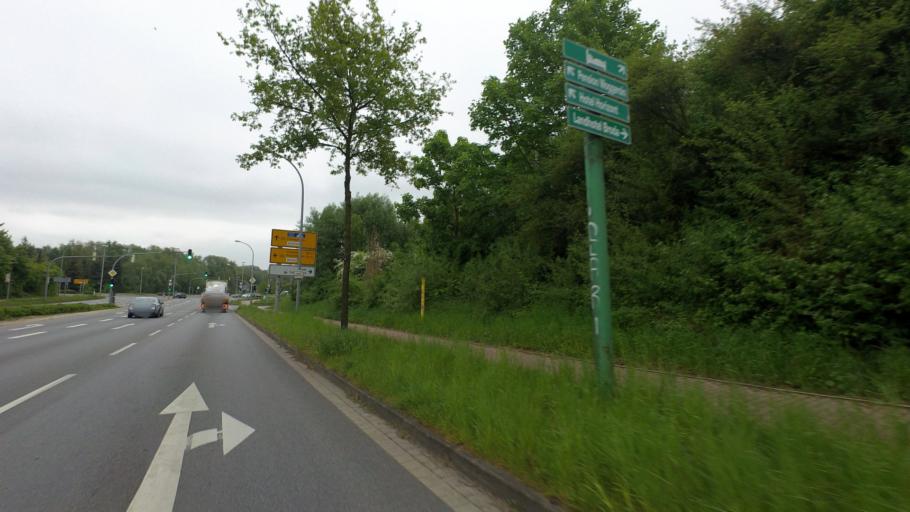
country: DE
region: Mecklenburg-Vorpommern
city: Neubrandenburg
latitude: 53.5563
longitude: 13.2331
